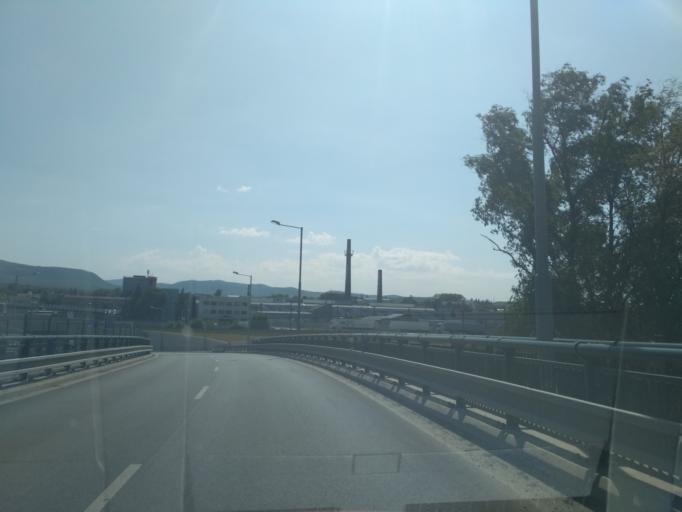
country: SK
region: Presovsky
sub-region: Okres Presov
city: Presov
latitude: 48.9695
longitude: 21.2489
